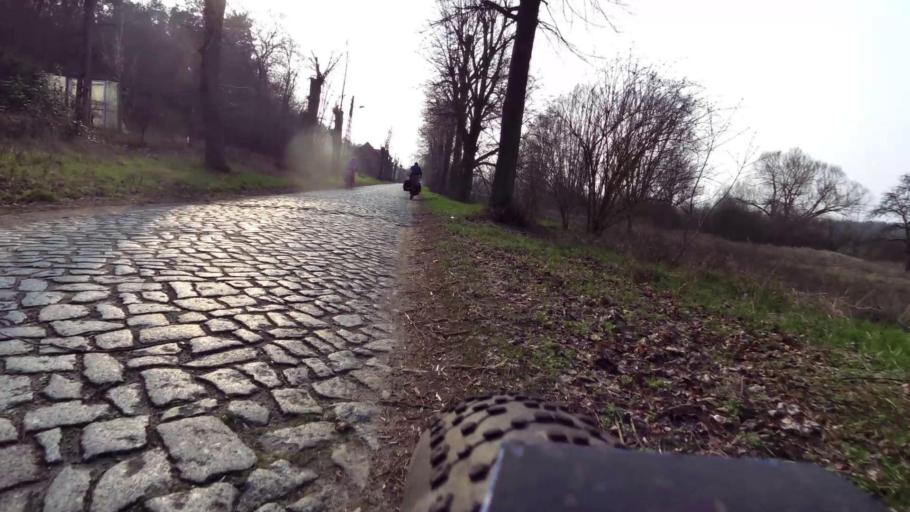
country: DE
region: Brandenburg
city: Vogelsang
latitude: 52.2480
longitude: 14.7213
